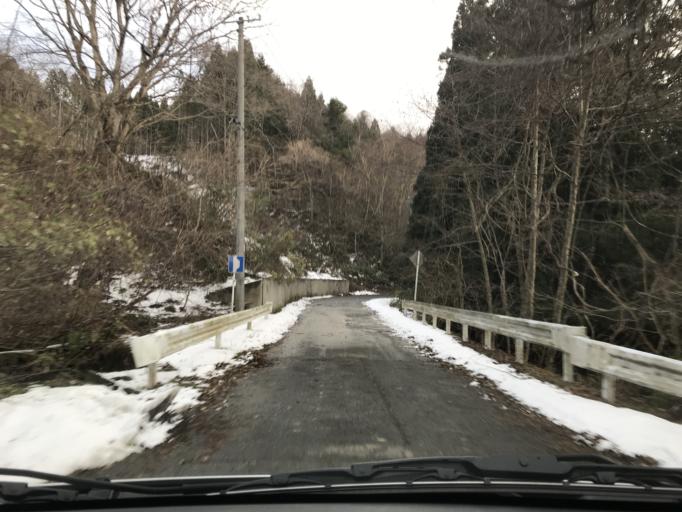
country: JP
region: Iwate
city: Ichinoseki
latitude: 39.0111
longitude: 140.9790
